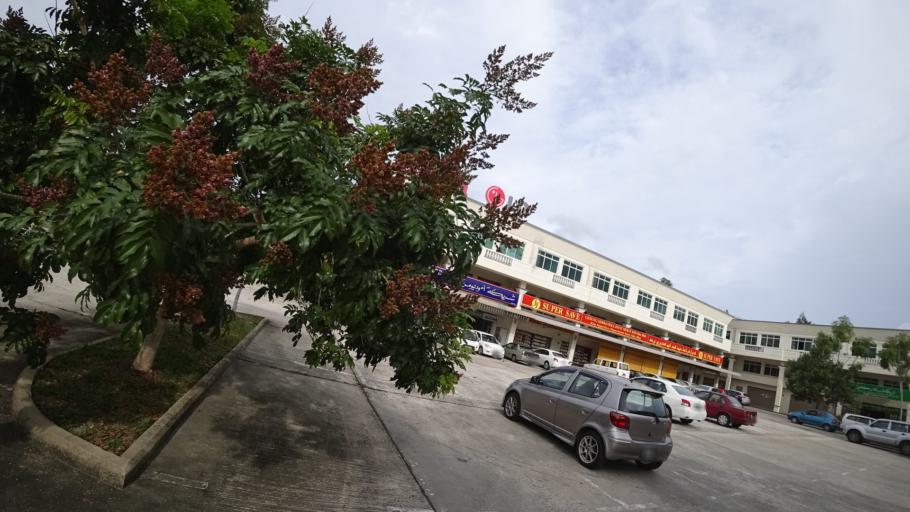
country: BN
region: Brunei and Muara
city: Bandar Seri Begawan
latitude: 4.8890
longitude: 114.8586
